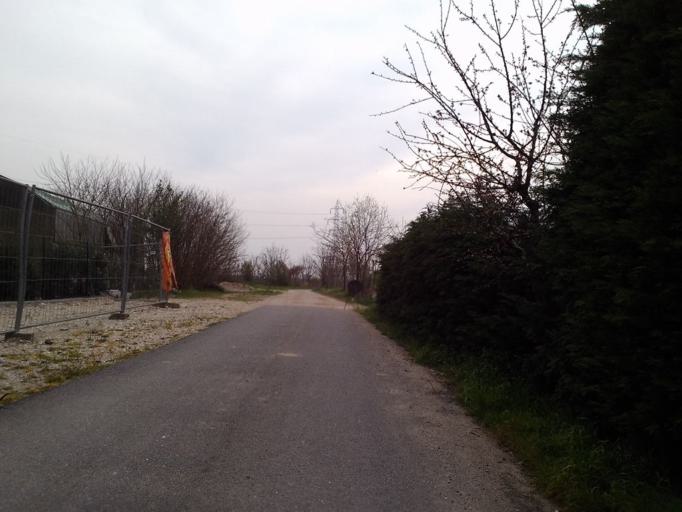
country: IT
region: Veneto
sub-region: Provincia di Verona
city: Povegliano Veronese
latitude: 45.3699
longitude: 10.8924
